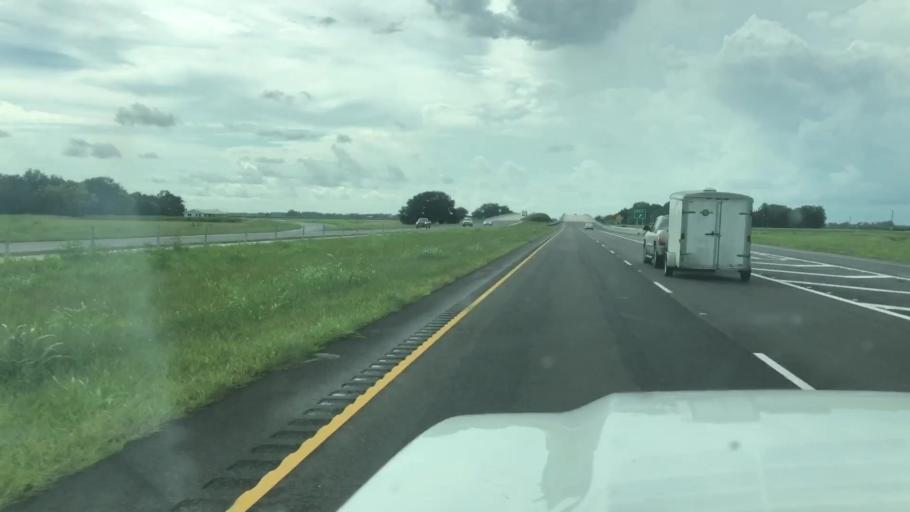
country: US
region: Louisiana
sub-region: Iberia Parish
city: Jeanerette
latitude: 29.8639
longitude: -91.6280
